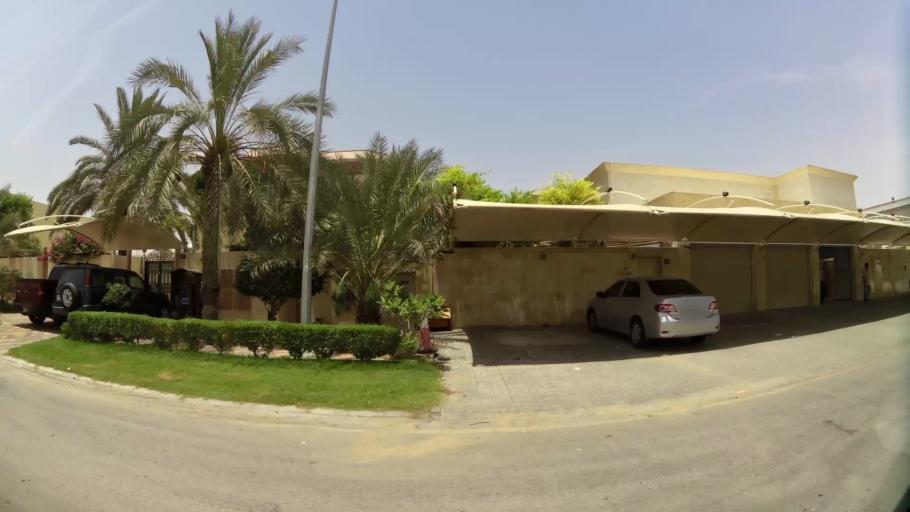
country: AE
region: Ash Shariqah
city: Sharjah
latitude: 25.2546
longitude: 55.4668
